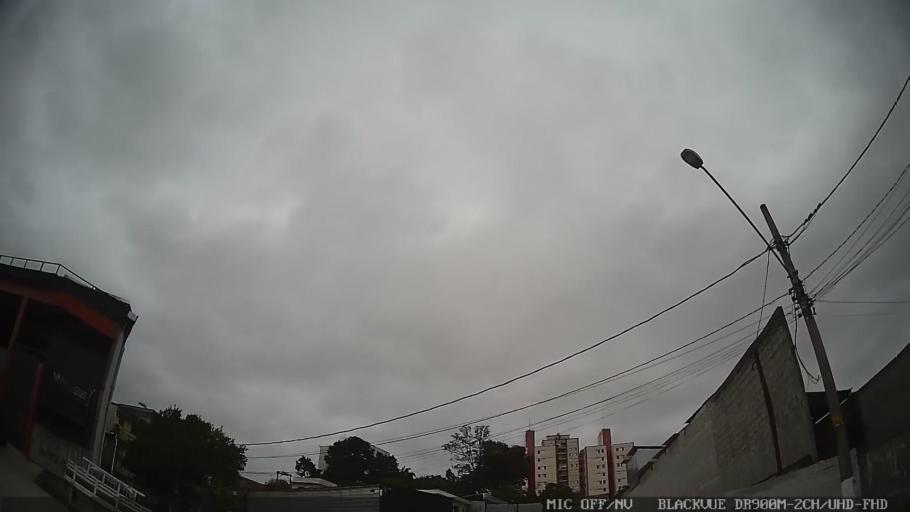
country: BR
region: Sao Paulo
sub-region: Osasco
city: Osasco
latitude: -23.5059
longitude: -46.7476
